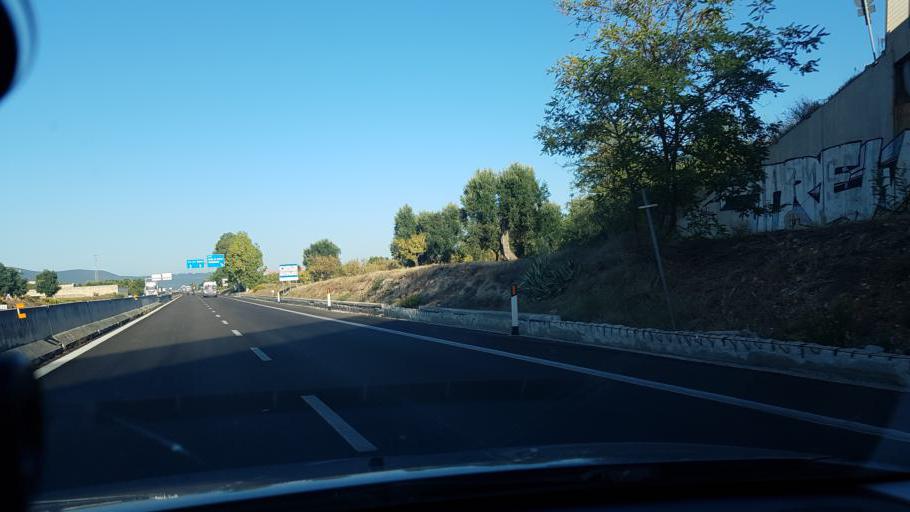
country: IT
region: Apulia
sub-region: Provincia di Brindisi
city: Fasano
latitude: 40.8359
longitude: 17.3869
